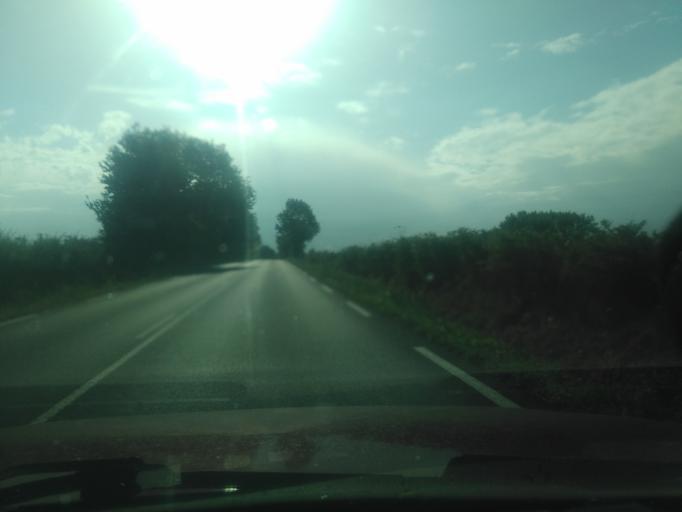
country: FR
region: Pays de la Loire
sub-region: Departement de la Vendee
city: Mouilleron-en-Pareds
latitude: 46.6764
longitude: -0.8772
